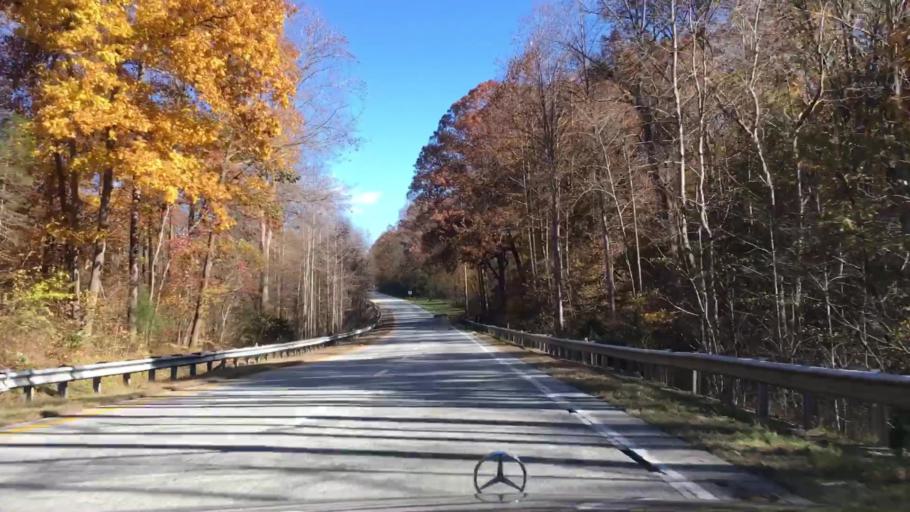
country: US
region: Virginia
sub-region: Nelson County
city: Nellysford
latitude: 37.8429
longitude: -78.7794
